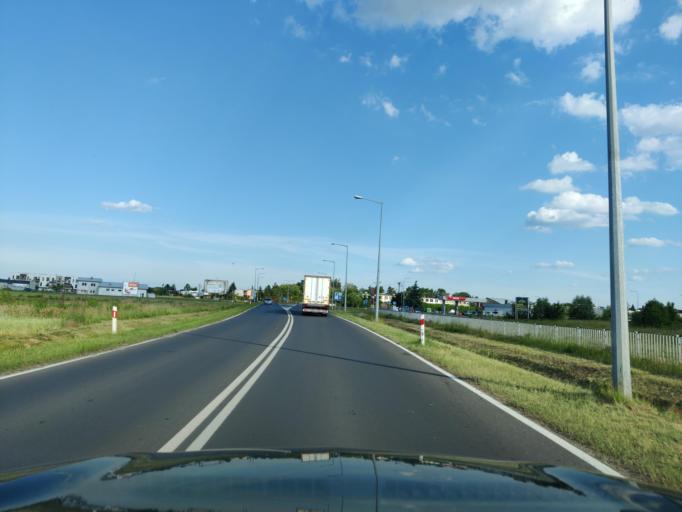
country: PL
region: Greater Poland Voivodeship
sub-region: Powiat wolsztynski
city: Wolsztyn
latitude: 52.1227
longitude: 16.1263
